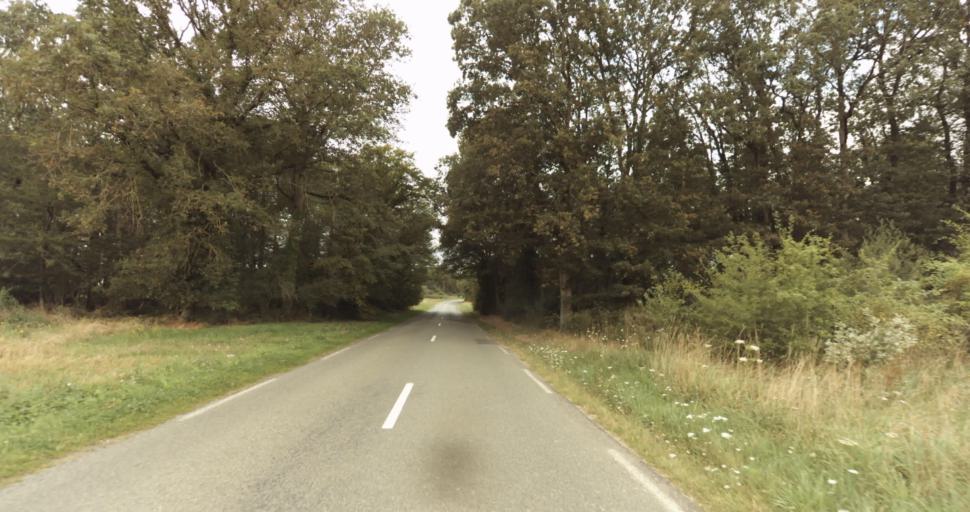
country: FR
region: Haute-Normandie
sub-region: Departement de l'Eure
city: Menilles
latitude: 48.9807
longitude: 1.2719
